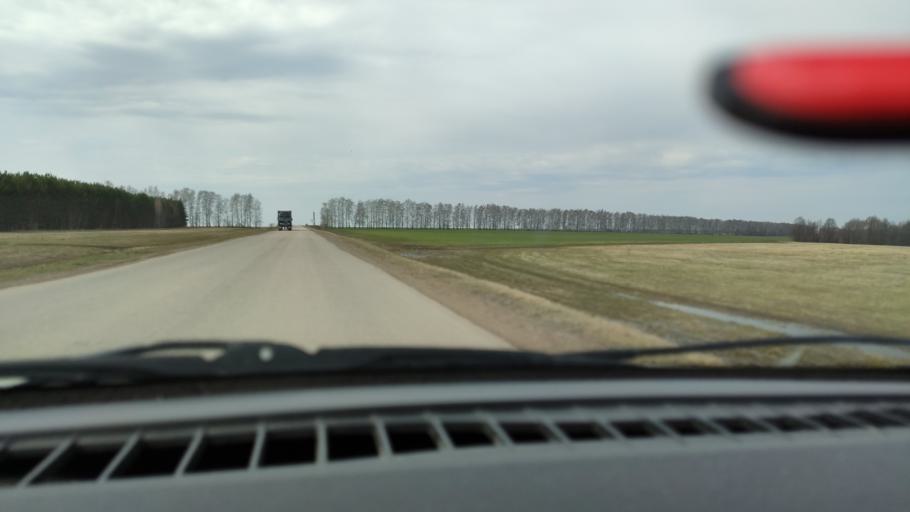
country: RU
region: Bashkortostan
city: Dyurtyuli
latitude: 55.6620
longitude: 55.0609
